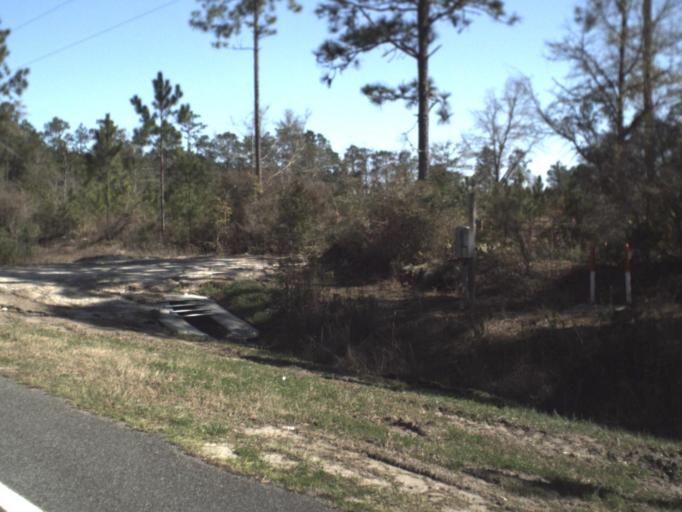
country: US
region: Florida
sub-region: Bay County
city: Youngstown
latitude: 30.4357
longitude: -85.4318
